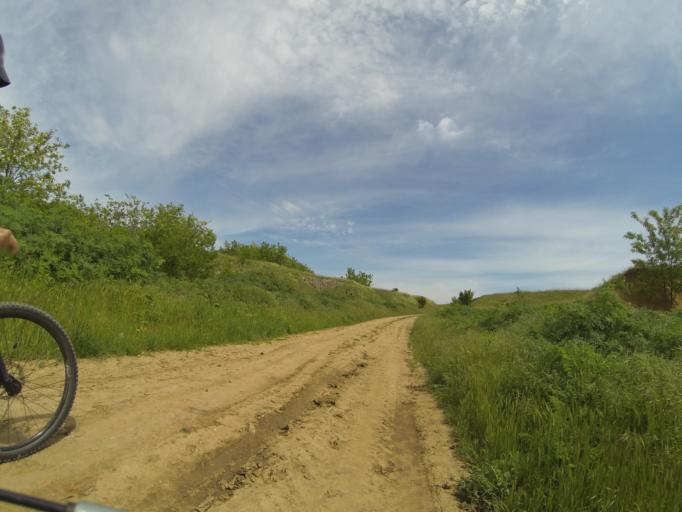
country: RO
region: Dolj
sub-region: Comuna Leu
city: Leu
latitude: 44.2001
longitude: 23.9925
